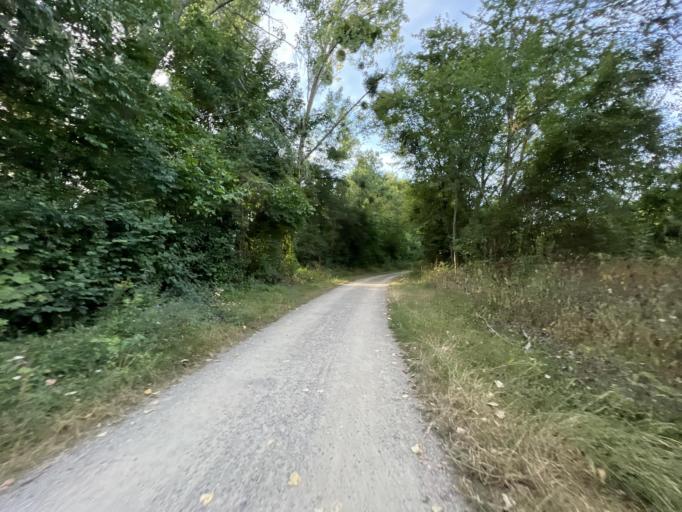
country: DE
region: North Rhine-Westphalia
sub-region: Regierungsbezirk Koln
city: Kreuzau
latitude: 50.7754
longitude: 6.4826
